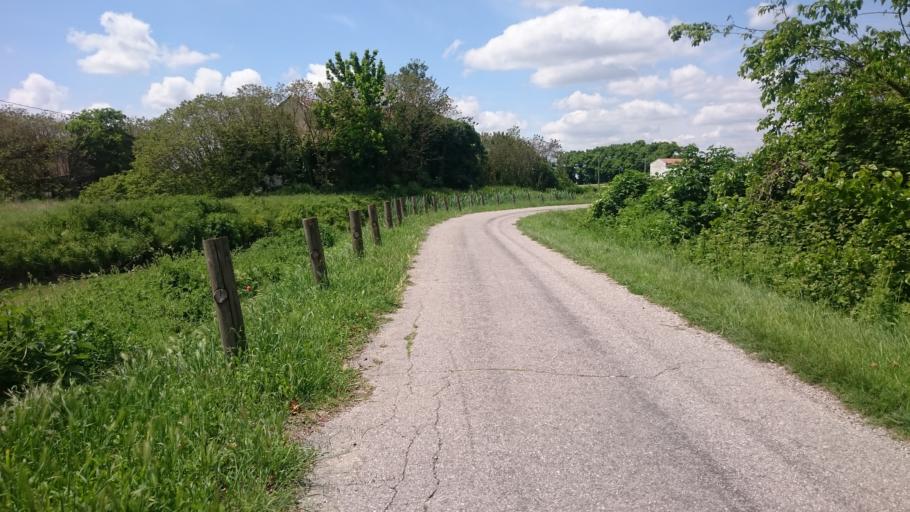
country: IT
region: Lombardy
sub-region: Provincia di Mantova
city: San Biagio
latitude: 45.1055
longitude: 10.8340
